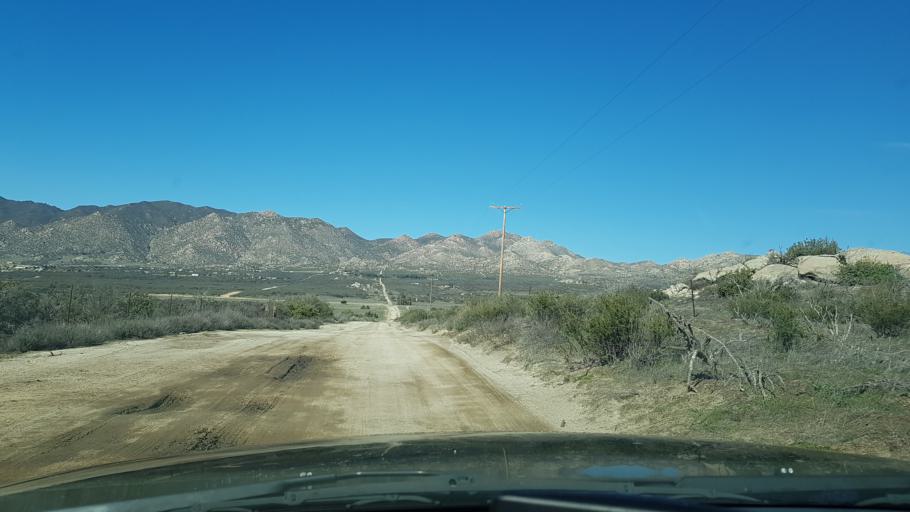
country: US
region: California
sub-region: San Diego County
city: Borrego Springs
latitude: 33.2030
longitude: -116.5082
